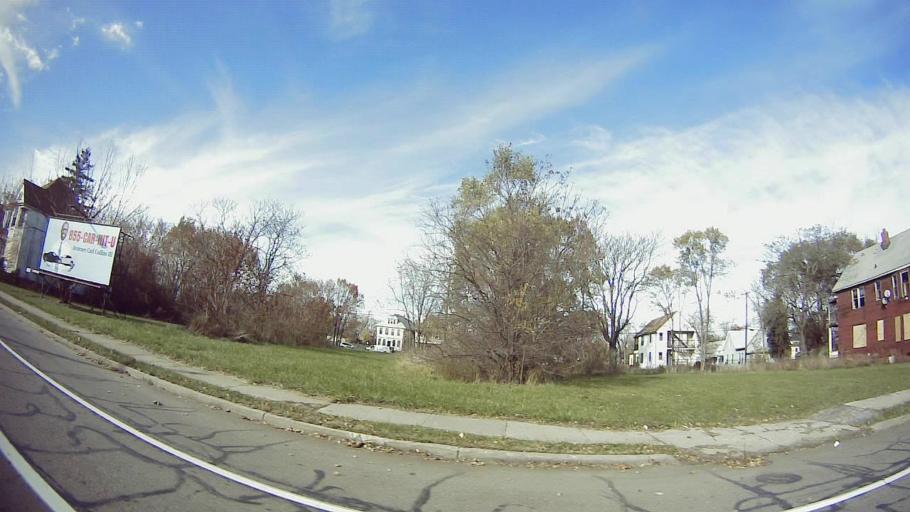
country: US
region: Michigan
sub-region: Wayne County
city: Hamtramck
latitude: 42.3700
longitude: -83.0291
